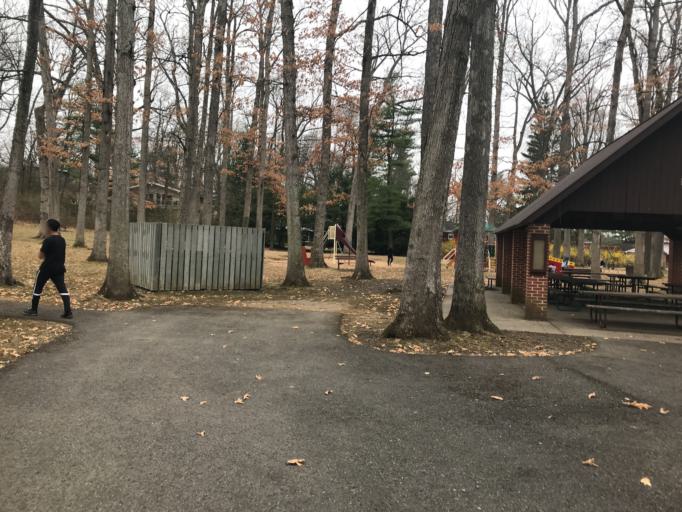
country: US
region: Pennsylvania
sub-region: Centre County
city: State College
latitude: 40.8039
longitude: -77.8749
